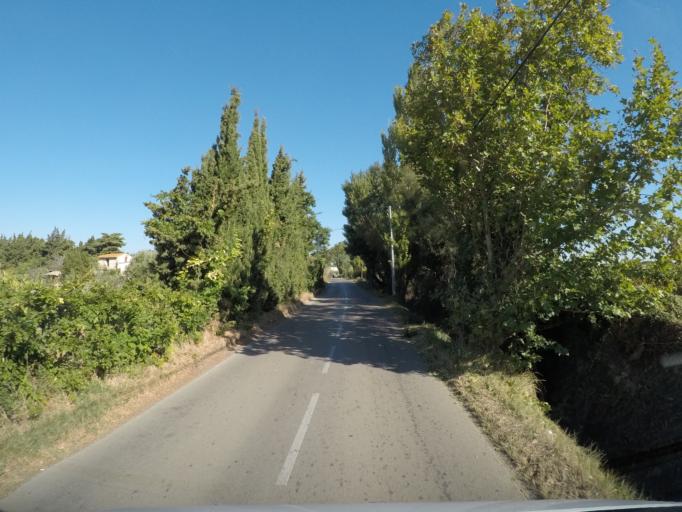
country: FR
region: Languedoc-Roussillon
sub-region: Departement de l'Aude
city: Narbonne
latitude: 43.1667
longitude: 3.0100
